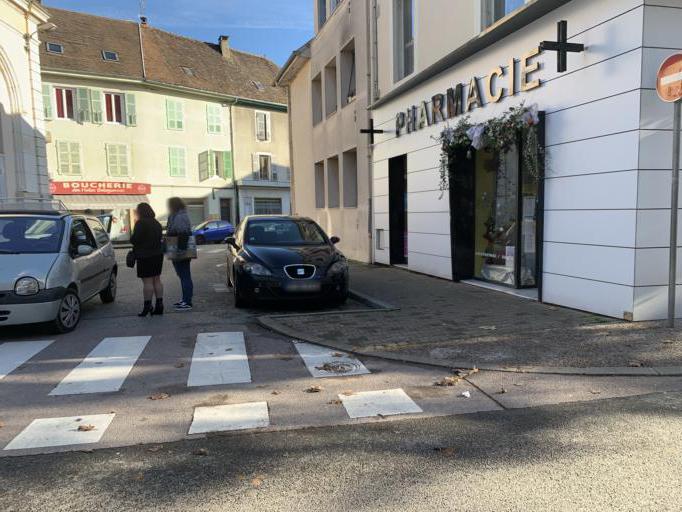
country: FR
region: Rhone-Alpes
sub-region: Departement de l'Ain
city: Belley
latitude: 45.7595
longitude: 5.6862
